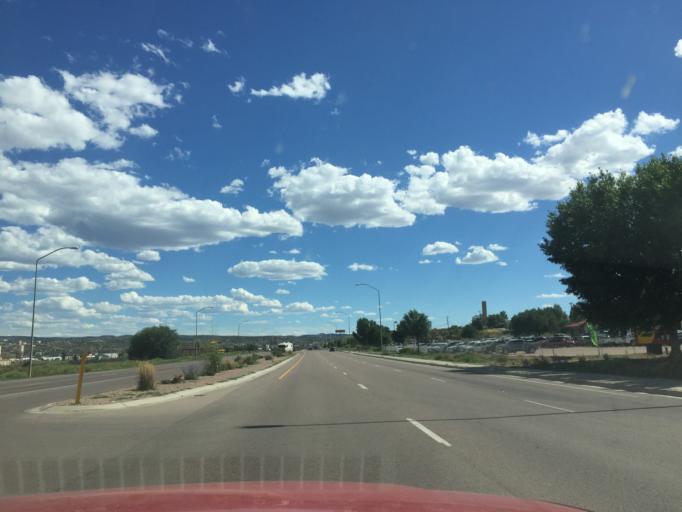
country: US
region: New Mexico
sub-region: McKinley County
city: Gallup
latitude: 35.5463
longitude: -108.7589
